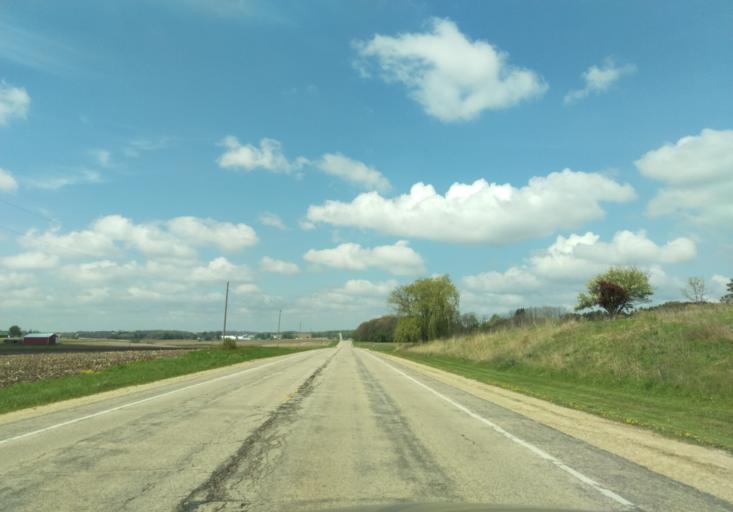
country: US
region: Wisconsin
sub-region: Dane County
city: Cross Plains
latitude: 43.0605
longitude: -89.6287
